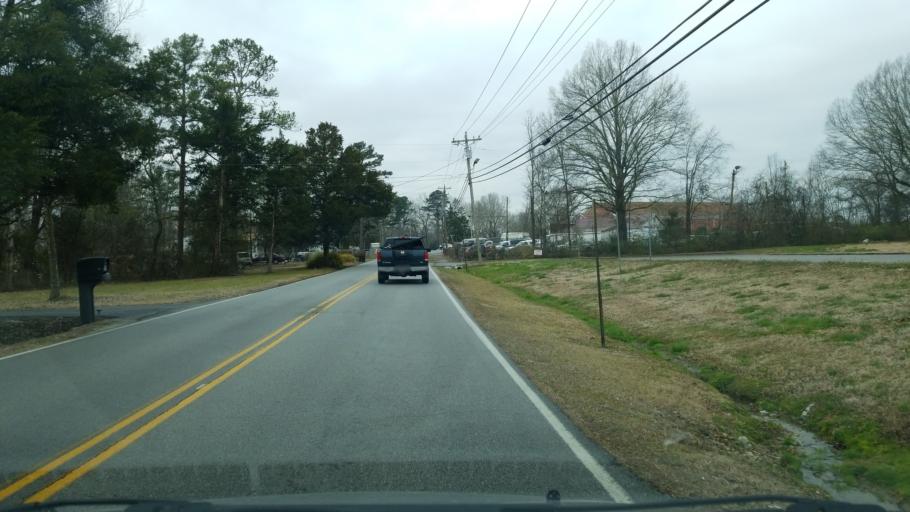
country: US
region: Georgia
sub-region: Catoosa County
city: Indian Springs
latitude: 34.9704
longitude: -85.1562
